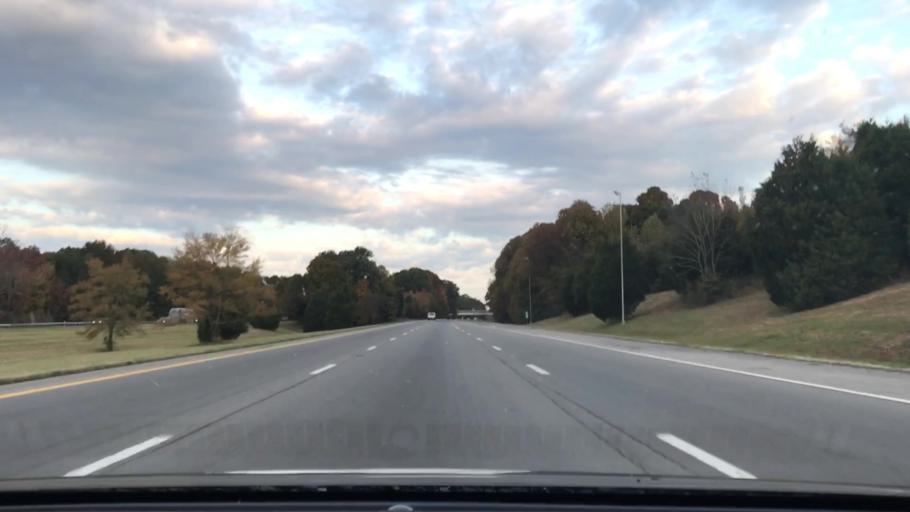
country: US
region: Tennessee
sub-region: Cheatham County
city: Pleasant View
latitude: 36.4059
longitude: -87.0313
